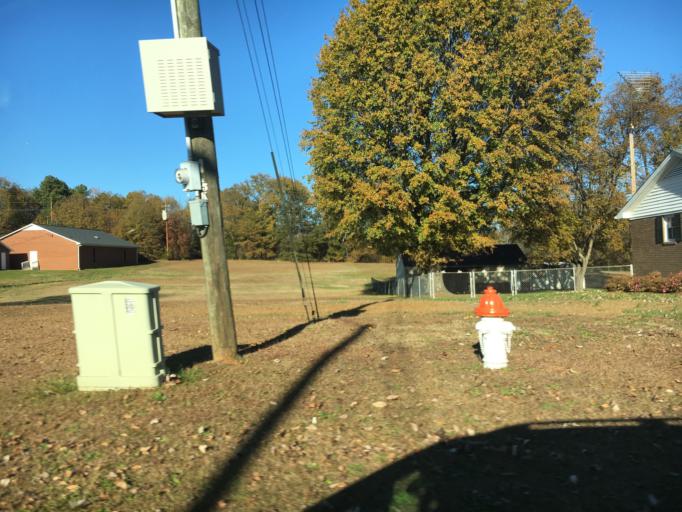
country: US
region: South Carolina
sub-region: Spartanburg County
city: Duncan
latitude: 34.9526
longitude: -82.1661
